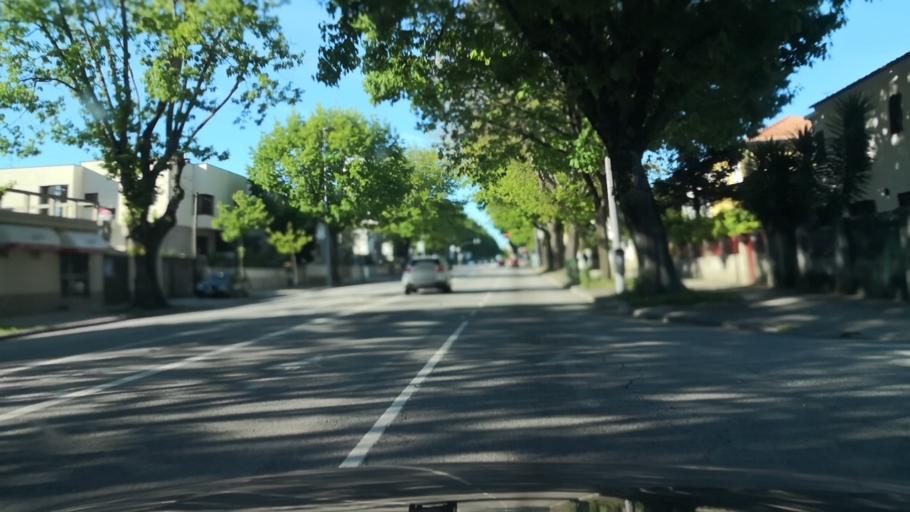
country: PT
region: Porto
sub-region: Maia
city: Pedroucos
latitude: 41.1727
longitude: -8.5854
